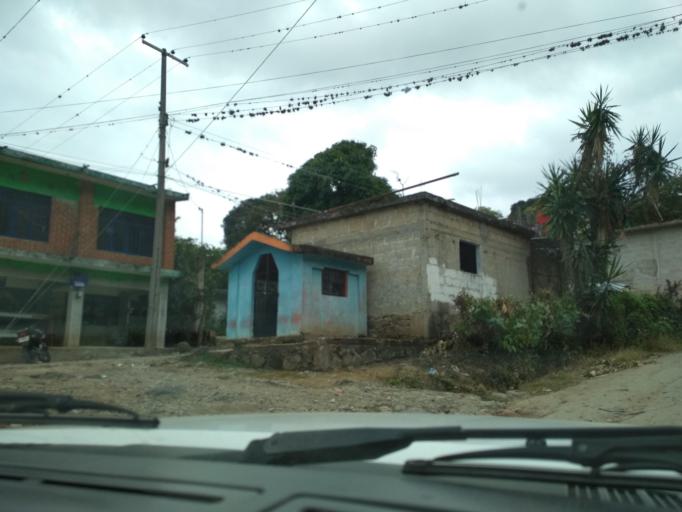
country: MX
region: Veracruz
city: El Castillo
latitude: 19.5822
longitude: -96.8703
